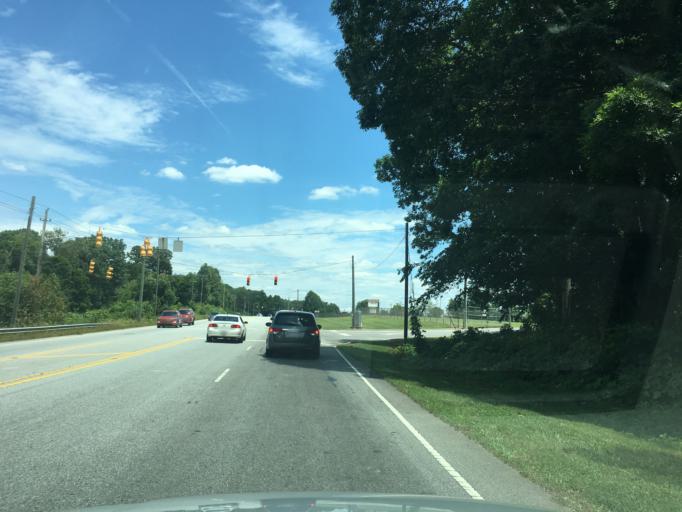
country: US
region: North Carolina
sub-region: Burke County
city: Morganton
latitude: 35.7432
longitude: -81.7227
